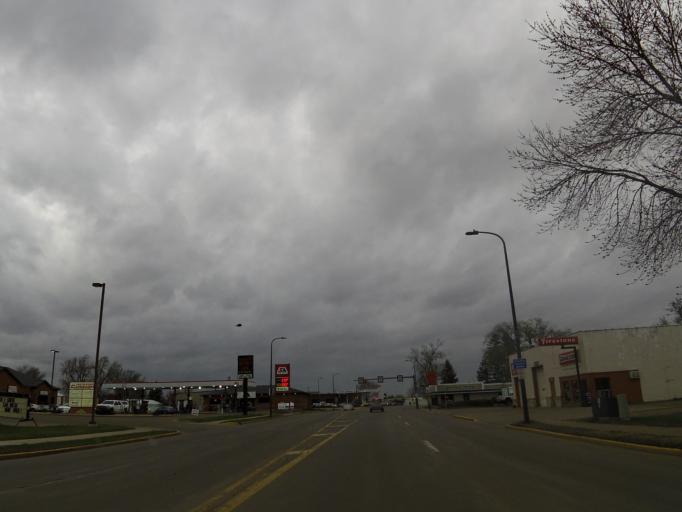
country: US
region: Wisconsin
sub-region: Saint Croix County
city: New Richmond
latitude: 45.1283
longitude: -92.5376
